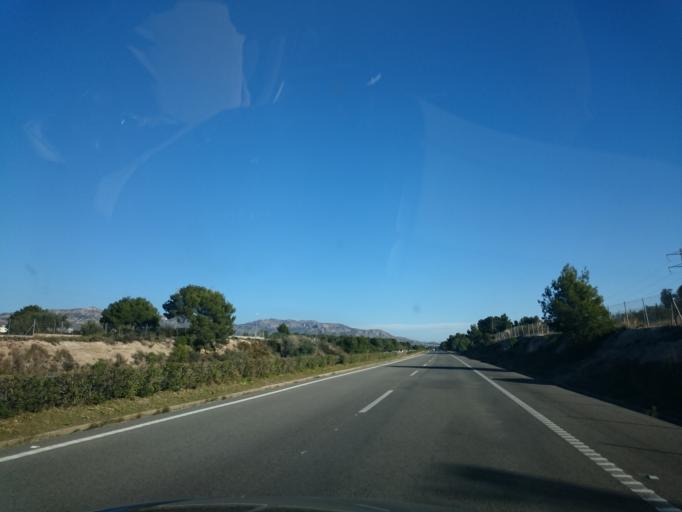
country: ES
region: Catalonia
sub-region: Provincia de Tarragona
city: l'Ametlla de Mar
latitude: 40.8998
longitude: 0.8125
